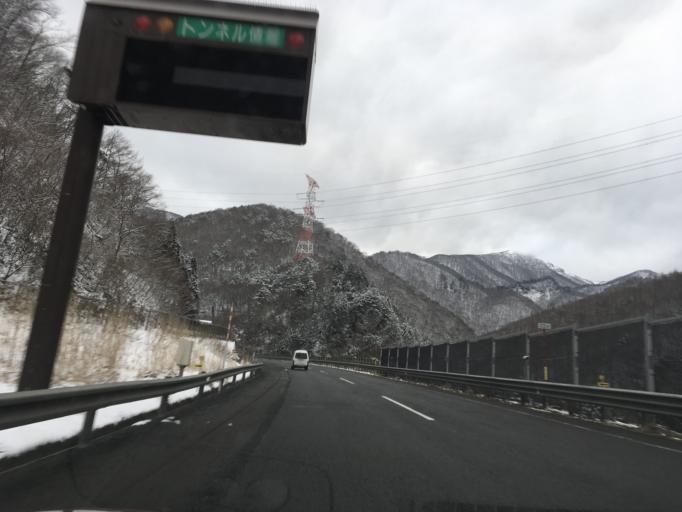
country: JP
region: Yamagata
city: Yamagata-shi
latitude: 38.2293
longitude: 140.4940
